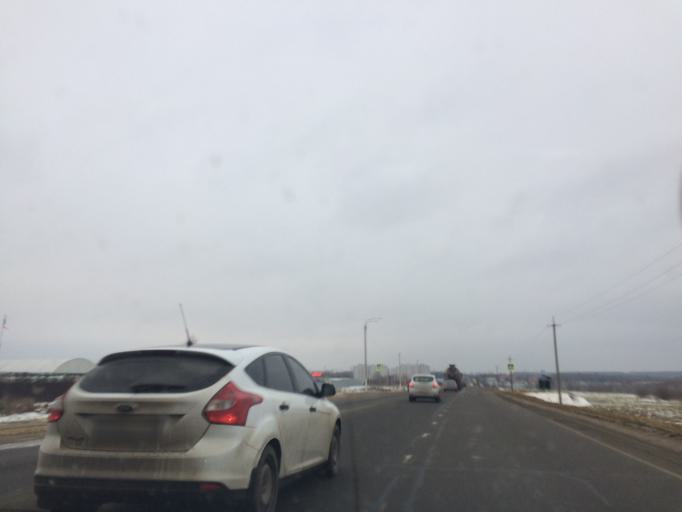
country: RU
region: Tula
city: Kosaya Gora
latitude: 54.1576
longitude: 37.4839
